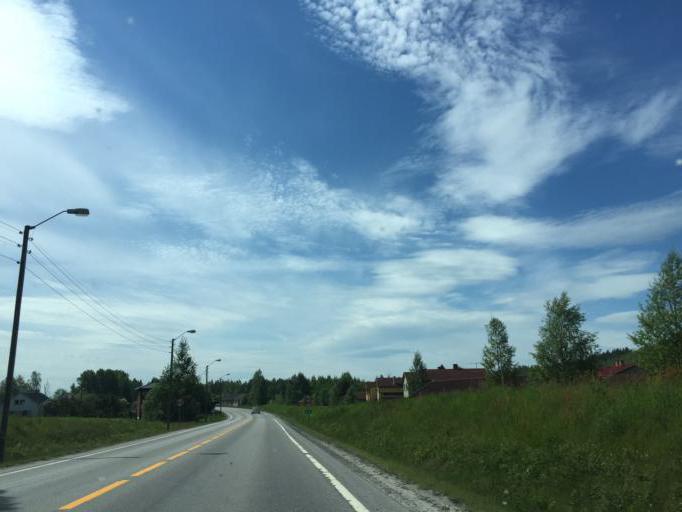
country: NO
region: Hedmark
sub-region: Sor-Odal
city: Skarnes
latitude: 60.2540
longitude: 11.6727
